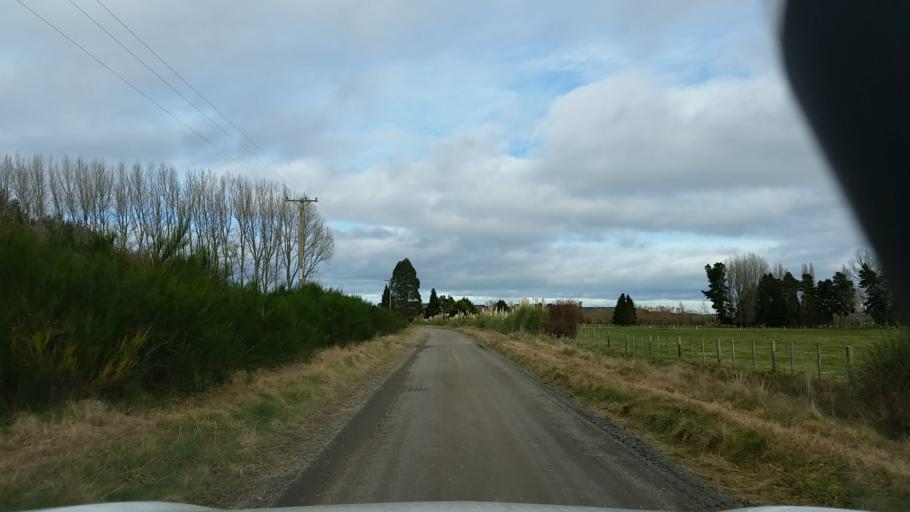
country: NZ
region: Bay of Plenty
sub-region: Whakatane District
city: Murupara
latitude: -38.2852
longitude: 176.5495
